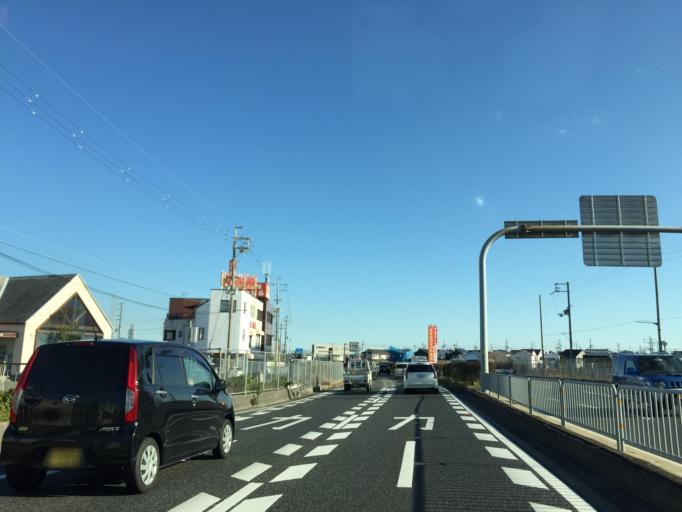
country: JP
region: Osaka
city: Kaizuka
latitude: 34.3621
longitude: 135.2725
